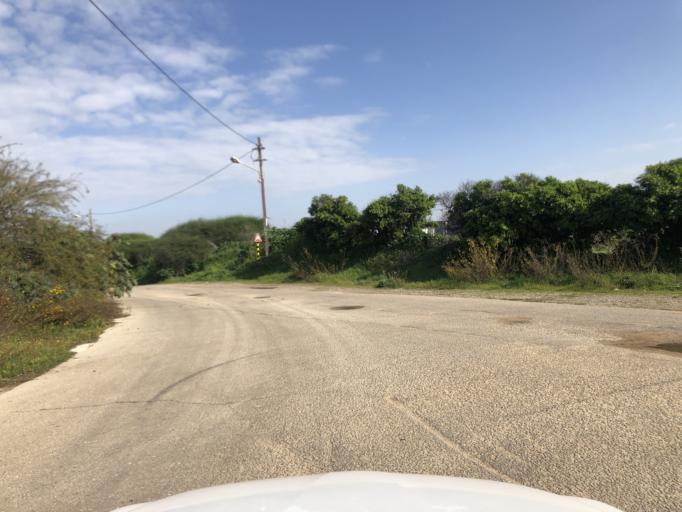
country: IL
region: Central District
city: Ness Ziona
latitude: 31.9156
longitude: 34.7960
